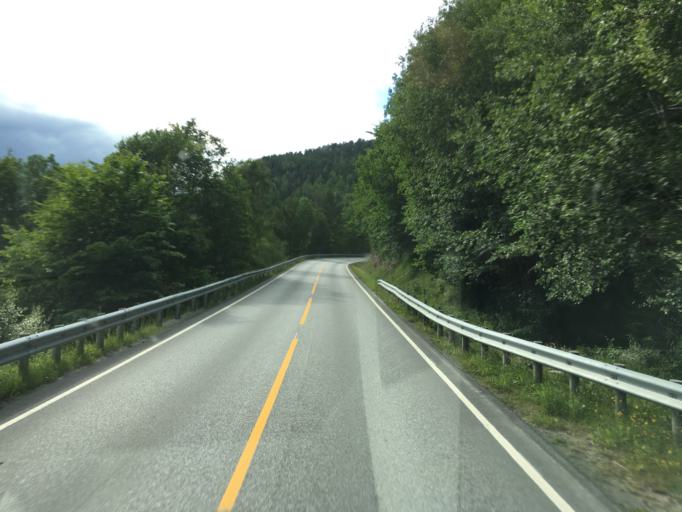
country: NO
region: More og Romsdal
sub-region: Tingvoll
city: Tingvoll
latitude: 62.9741
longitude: 8.0710
